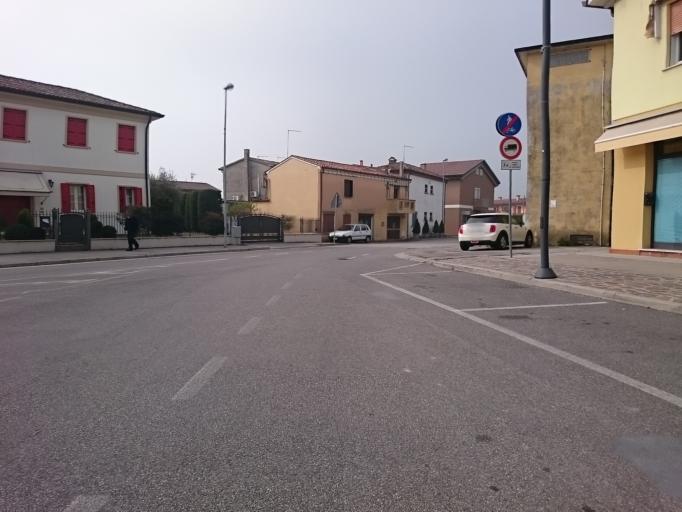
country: IT
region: Veneto
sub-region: Provincia di Padova
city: Bertipaglia
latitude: 45.3132
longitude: 11.8830
